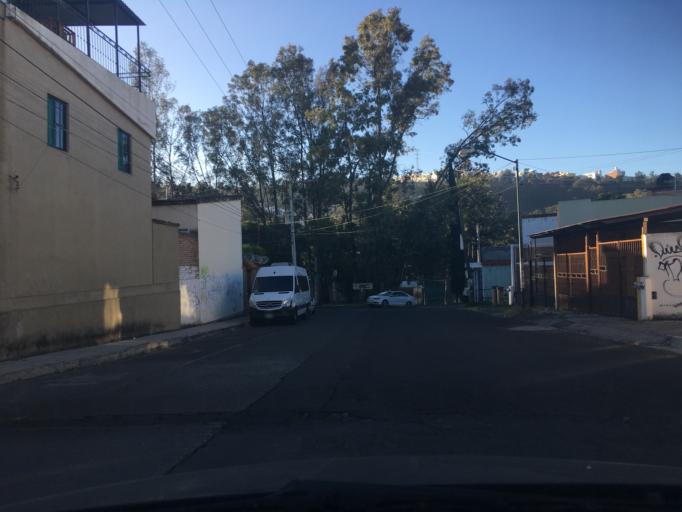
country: MX
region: Michoacan
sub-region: Morelia
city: Morelos
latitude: 19.6694
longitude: -101.2066
